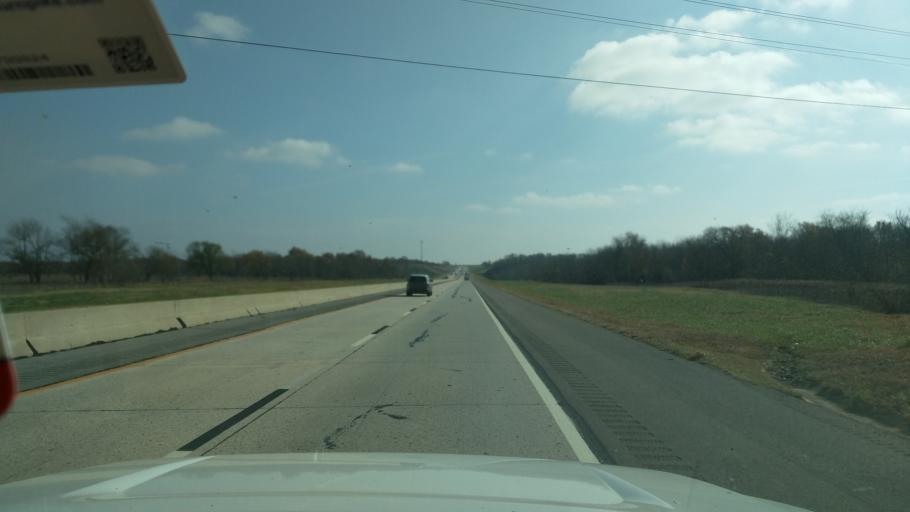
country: US
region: Oklahoma
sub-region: Wagoner County
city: Coweta
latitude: 35.8944
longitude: -95.5091
